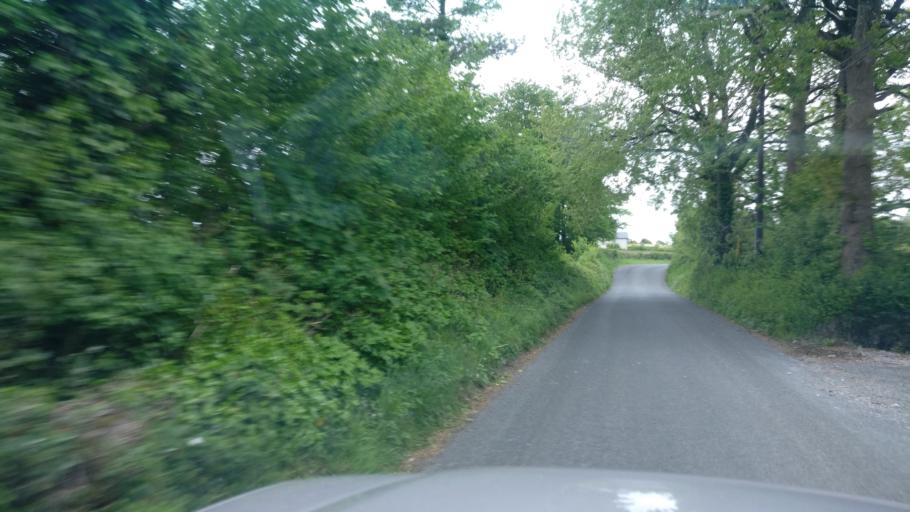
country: IE
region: Connaught
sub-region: County Galway
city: Loughrea
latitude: 53.1142
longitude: -8.4202
